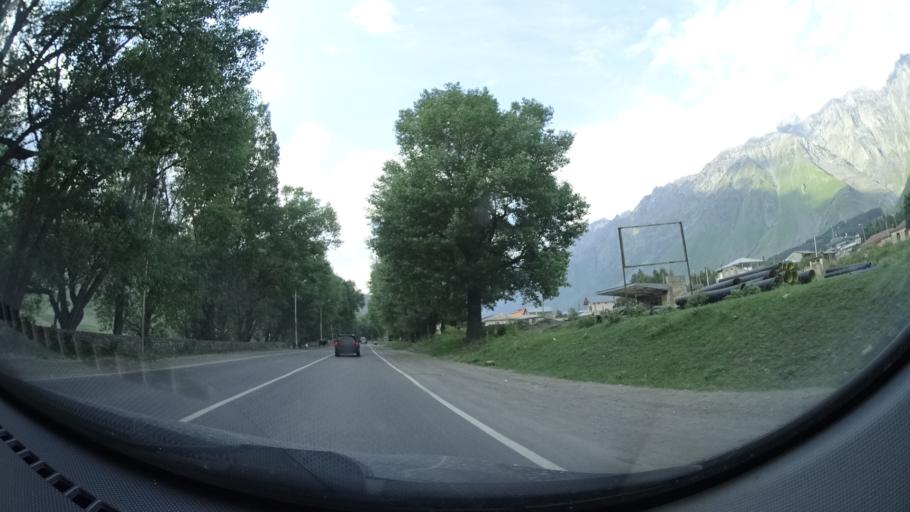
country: GE
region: Mtskheta-Mtianeti
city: Step'antsminda
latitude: 42.6511
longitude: 44.6410
